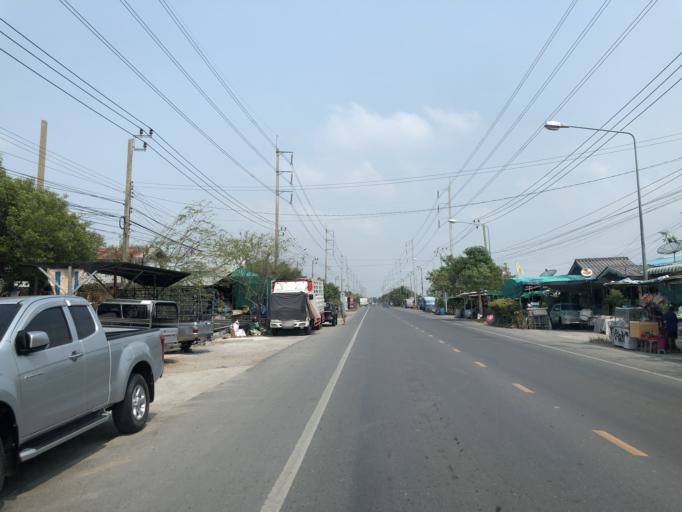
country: TH
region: Samut Prakan
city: Bang Bo
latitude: 13.5118
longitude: 100.8330
